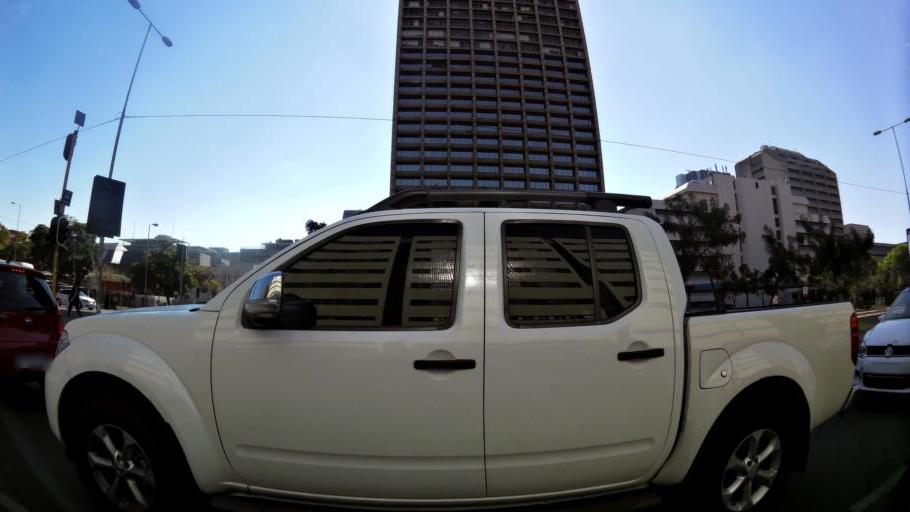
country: ZA
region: Gauteng
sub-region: City of Tshwane Metropolitan Municipality
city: Pretoria
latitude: -25.7507
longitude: 28.1910
